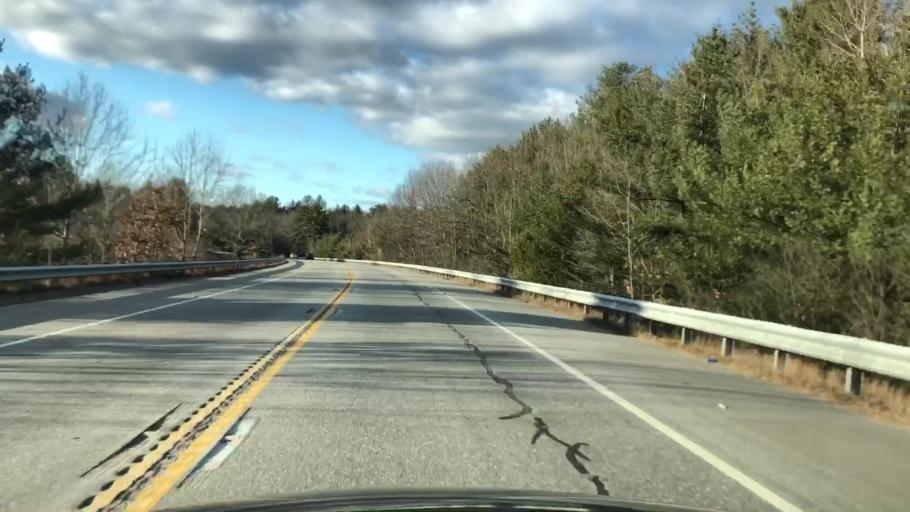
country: US
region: New Hampshire
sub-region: Hillsborough County
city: Milford
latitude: 42.8243
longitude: -71.6617
